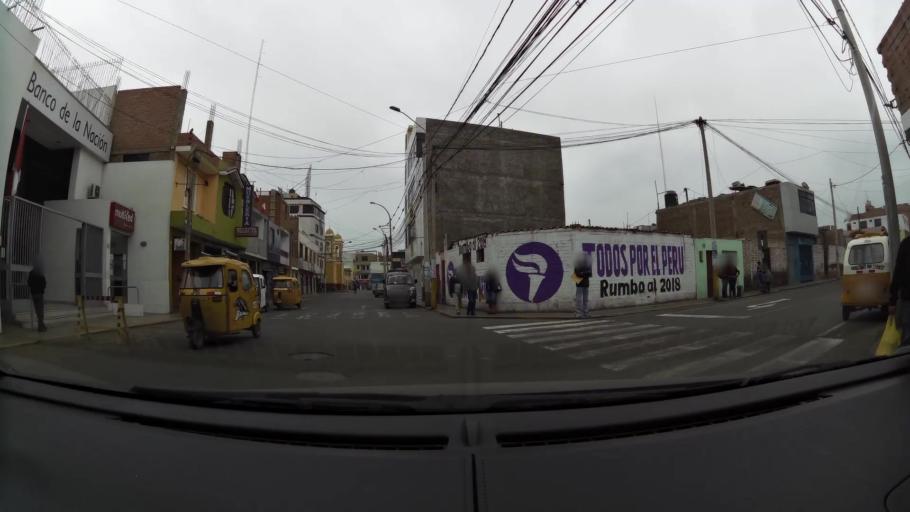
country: PE
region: Lima
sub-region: Barranca
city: Barranca
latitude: -10.7551
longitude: -77.7605
